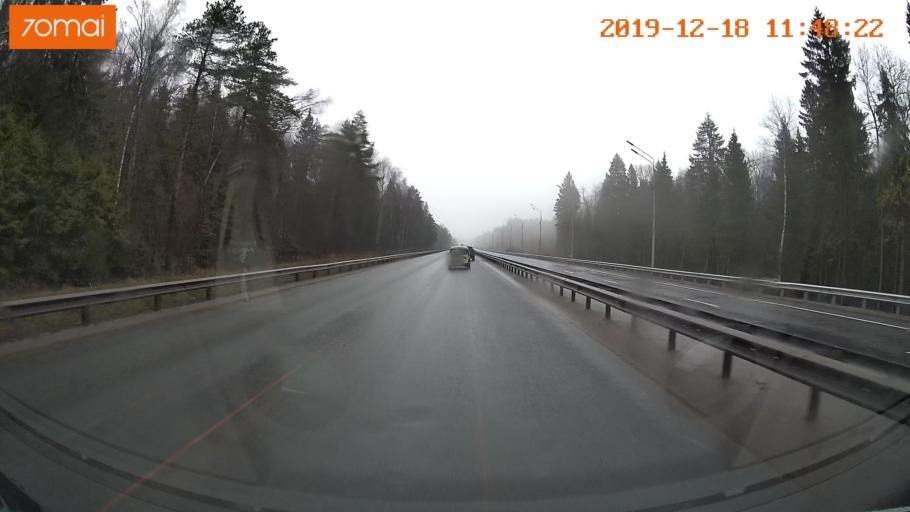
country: RU
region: Moskovskaya
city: Yershovo
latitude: 55.7674
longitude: 36.9028
